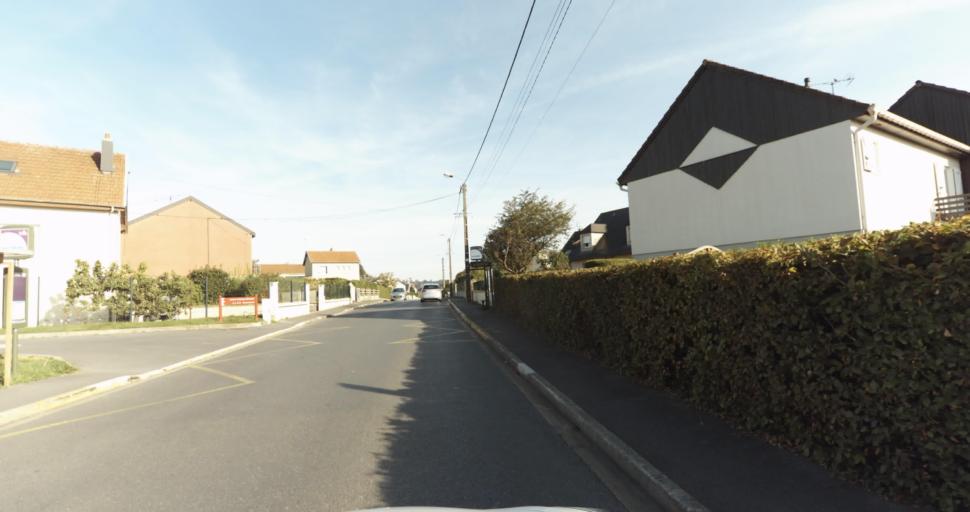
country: FR
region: Champagne-Ardenne
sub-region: Departement des Ardennes
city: Villers-Semeuse
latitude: 49.7423
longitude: 4.7484
